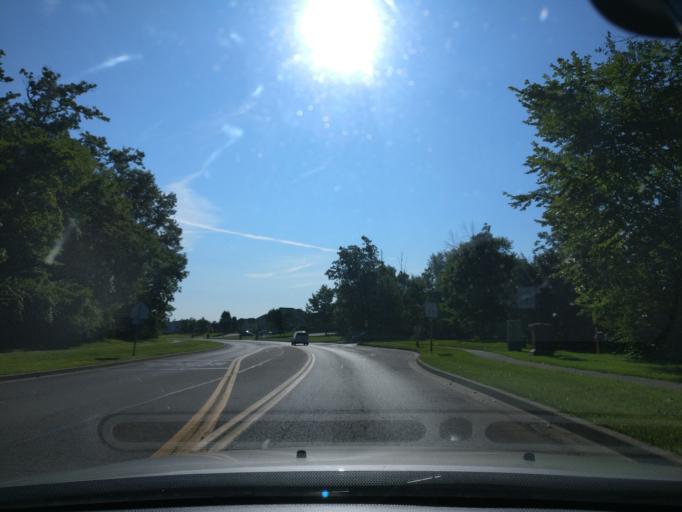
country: US
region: Ohio
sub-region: Warren County
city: Five Points
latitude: 39.6112
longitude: -84.2079
